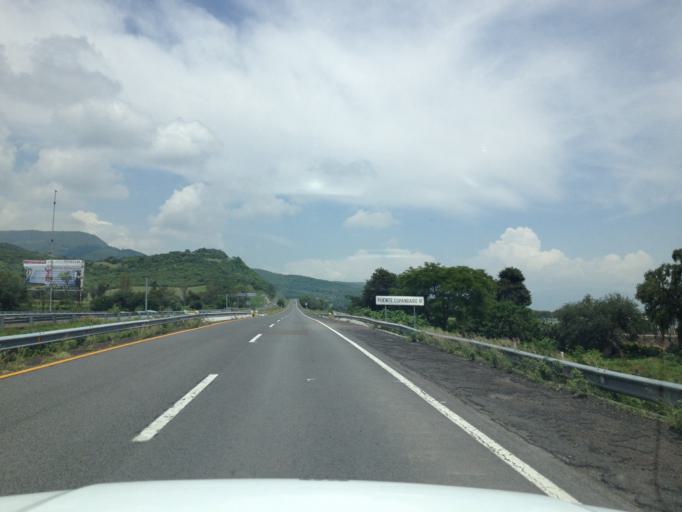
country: MX
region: Michoacan
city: Copandaro de Galeana
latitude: 19.8810
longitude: -101.2067
